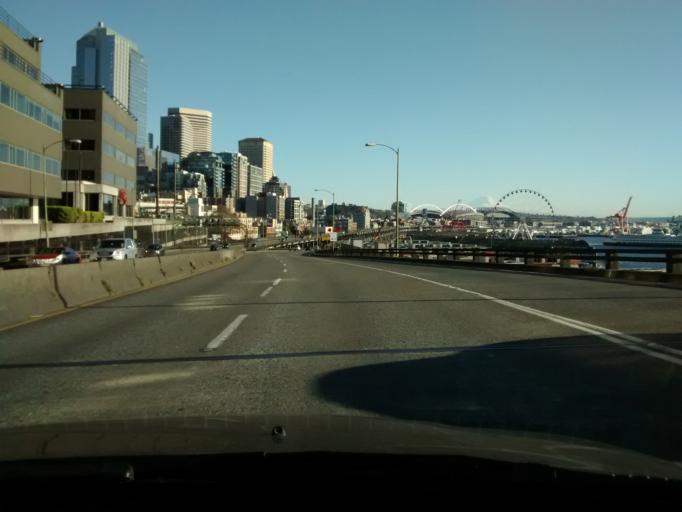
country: US
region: Washington
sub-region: King County
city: Seattle
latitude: 47.6109
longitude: -122.3457
